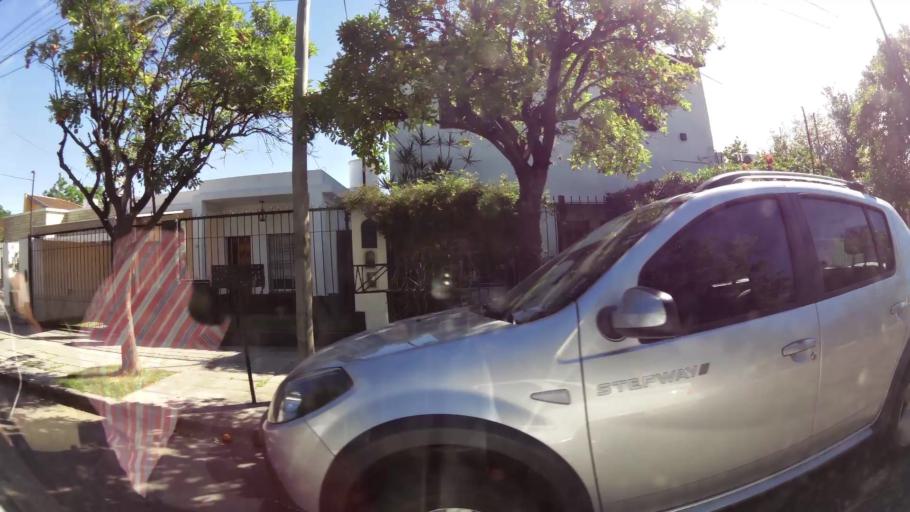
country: AR
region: Buenos Aires
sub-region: Partido de San Isidro
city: San Isidro
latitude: -34.5089
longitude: -58.5689
